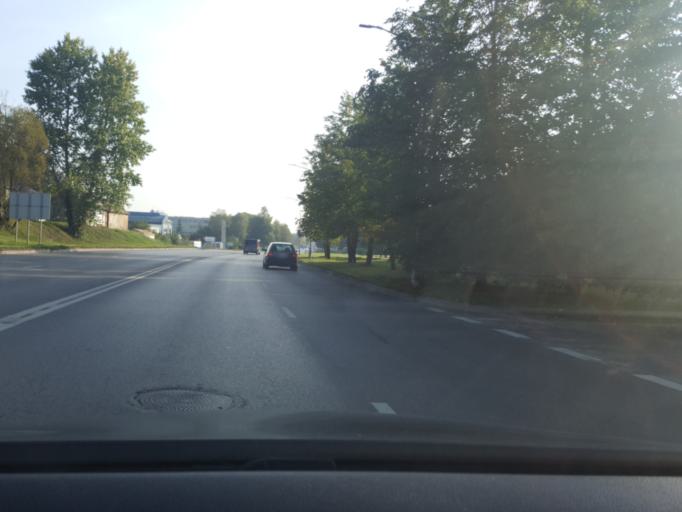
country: LT
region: Alytaus apskritis
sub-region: Alytus
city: Alytus
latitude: 54.4098
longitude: 24.0059
